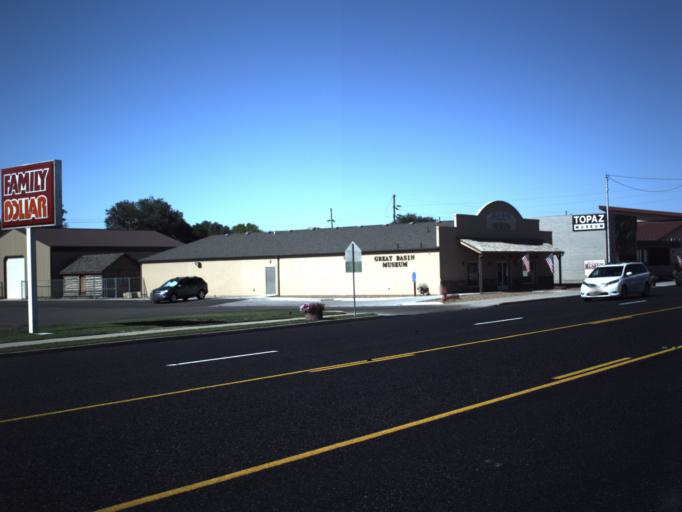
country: US
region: Utah
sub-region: Millard County
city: Delta
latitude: 39.3525
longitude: -112.5751
